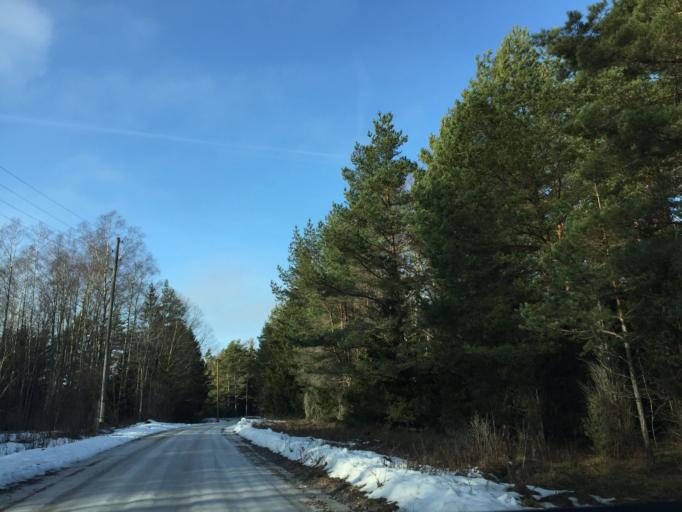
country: EE
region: Saare
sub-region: Kuressaare linn
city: Kuressaare
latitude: 58.4692
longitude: 21.9783
